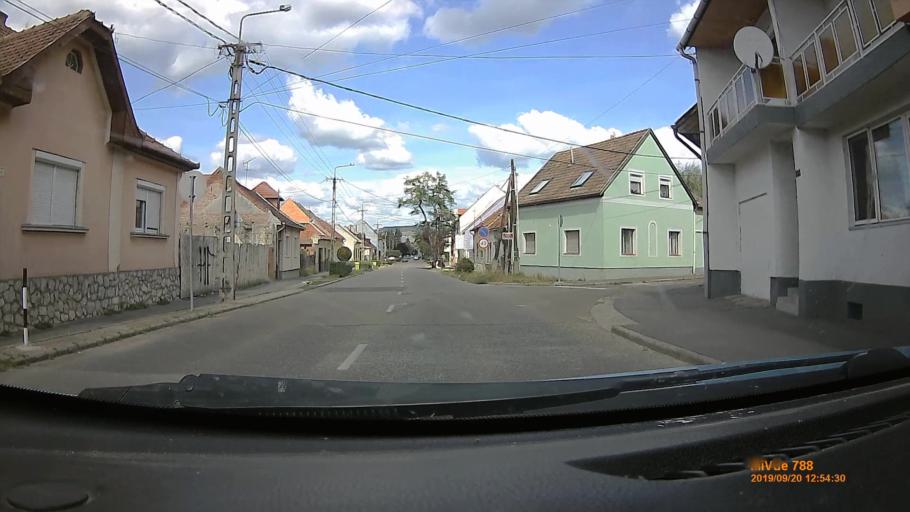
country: HU
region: Heves
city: Eger
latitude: 47.9111
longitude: 20.3766
